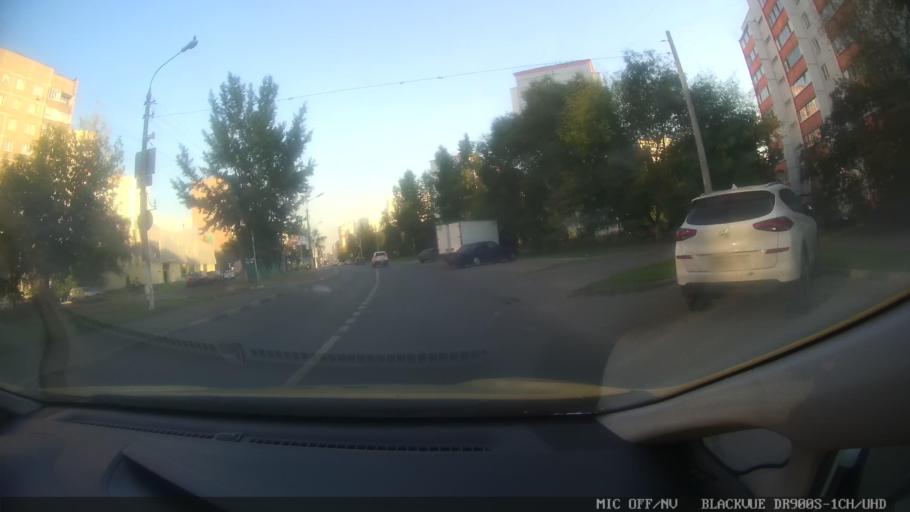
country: RU
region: Moscow
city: Nekrasovka
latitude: 55.6951
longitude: 37.9020
